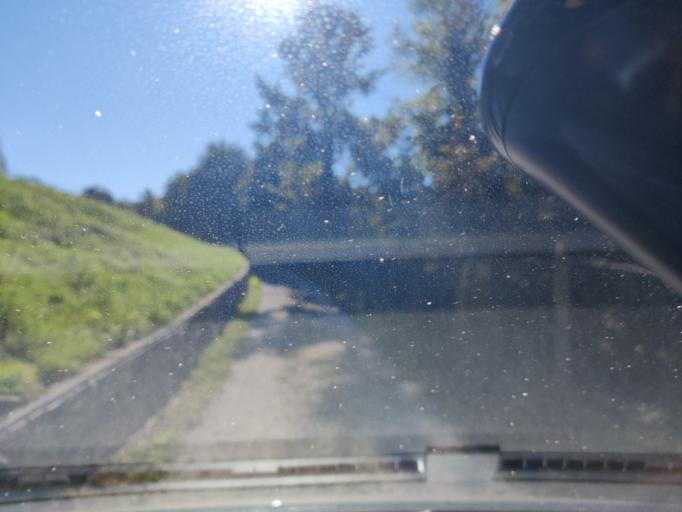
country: IT
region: Lombardy
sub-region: Provincia di Brescia
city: Capovalle
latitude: 45.7555
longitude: 10.5300
